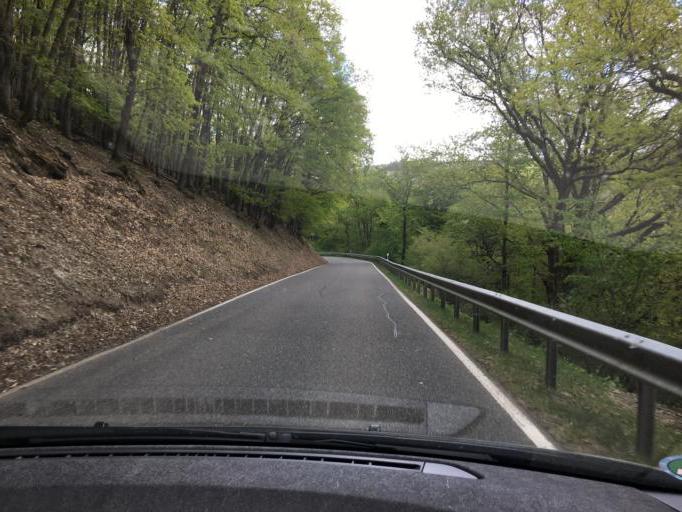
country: DE
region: Rheinland-Pfalz
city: Ahrbruck
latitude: 50.4887
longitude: 6.9601
